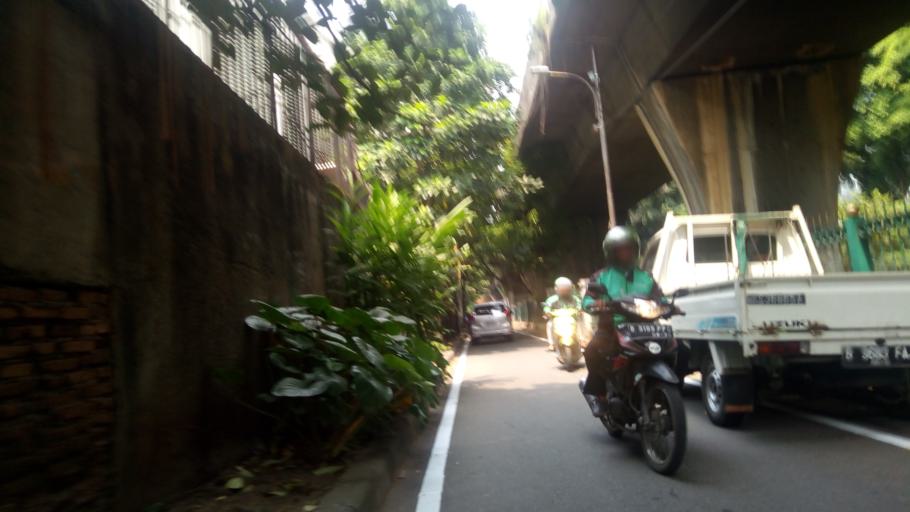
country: ID
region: Jakarta Raya
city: Jakarta
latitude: -6.1958
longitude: 106.8394
